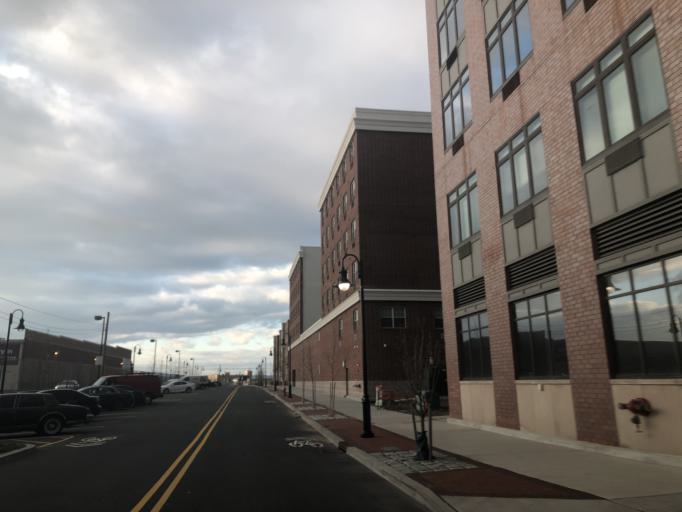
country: US
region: New Jersey
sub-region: Hudson County
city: Jersey City
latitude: 40.7110
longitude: -74.0946
